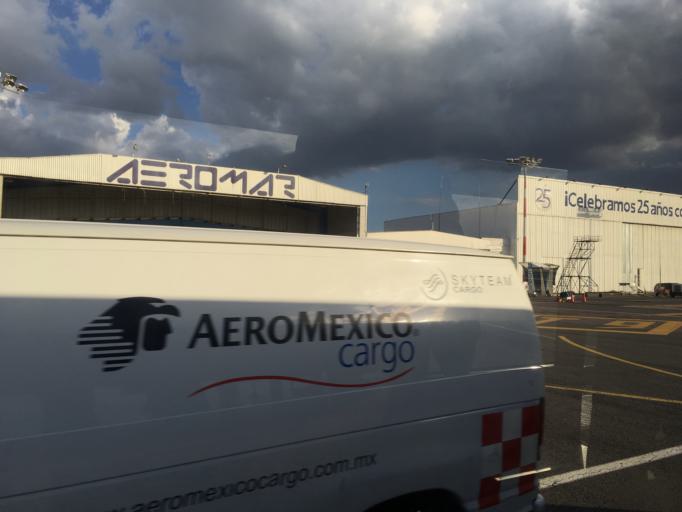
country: MX
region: Mexico City
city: Venustiano Carranza
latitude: 19.4277
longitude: -99.0769
